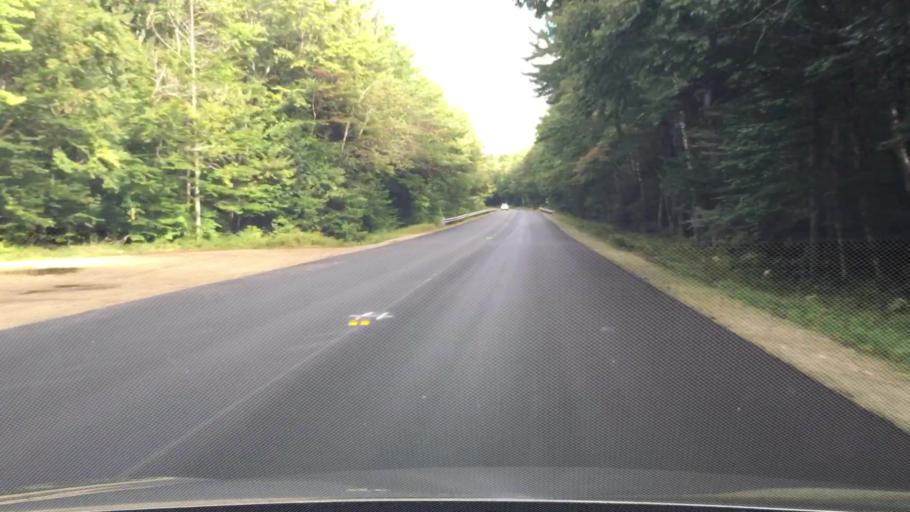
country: US
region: New Hampshire
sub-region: Carroll County
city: Tamworth
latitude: 43.9991
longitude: -71.3997
